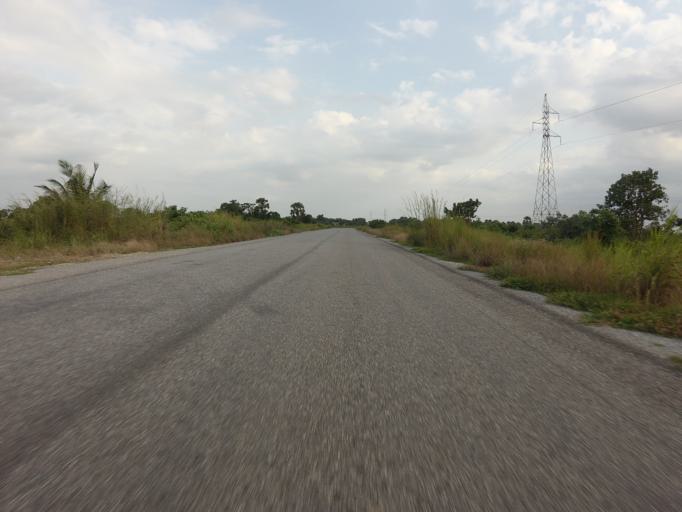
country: GH
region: Volta
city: Ho
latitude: 6.4002
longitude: 0.5251
